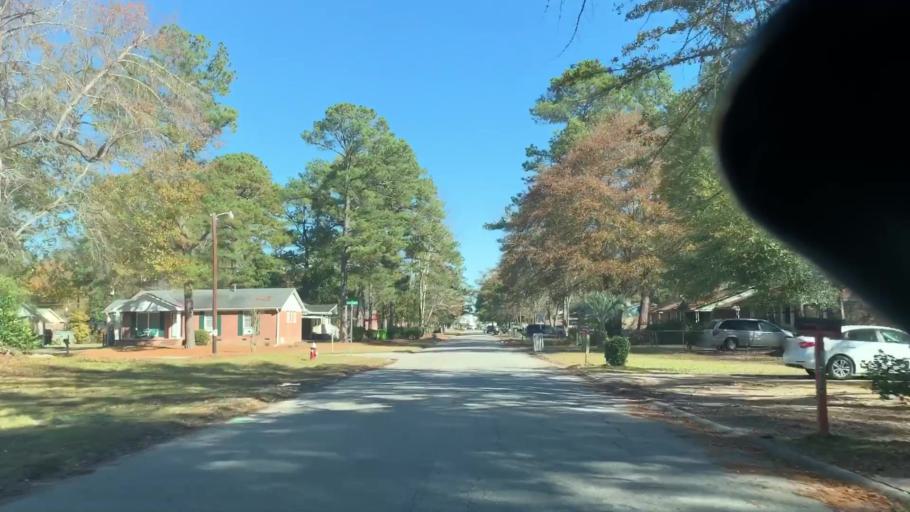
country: US
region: South Carolina
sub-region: Richland County
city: Forest Acres
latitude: 33.9344
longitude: -80.9665
